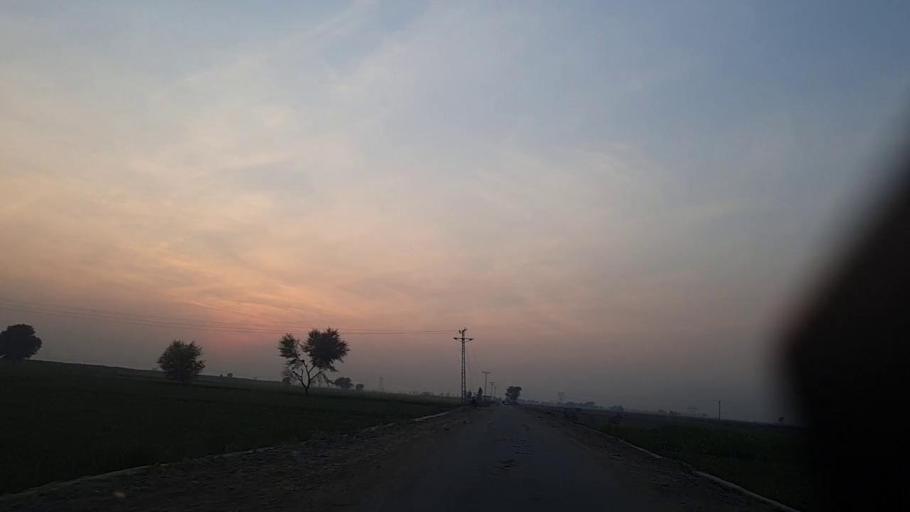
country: PK
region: Sindh
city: Sakrand
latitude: 26.0992
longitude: 68.3382
